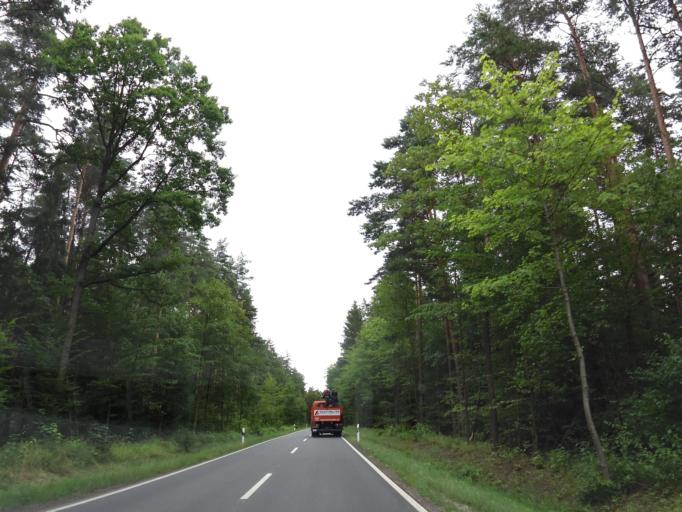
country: DE
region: Thuringia
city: Hainspitz
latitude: 50.9436
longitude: 11.8553
